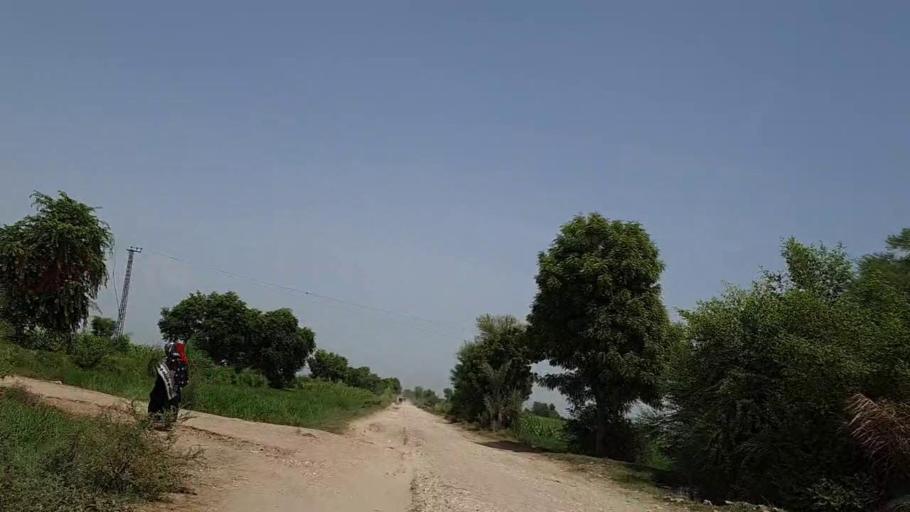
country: PK
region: Sindh
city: Tharu Shah
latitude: 26.8992
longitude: 68.0081
